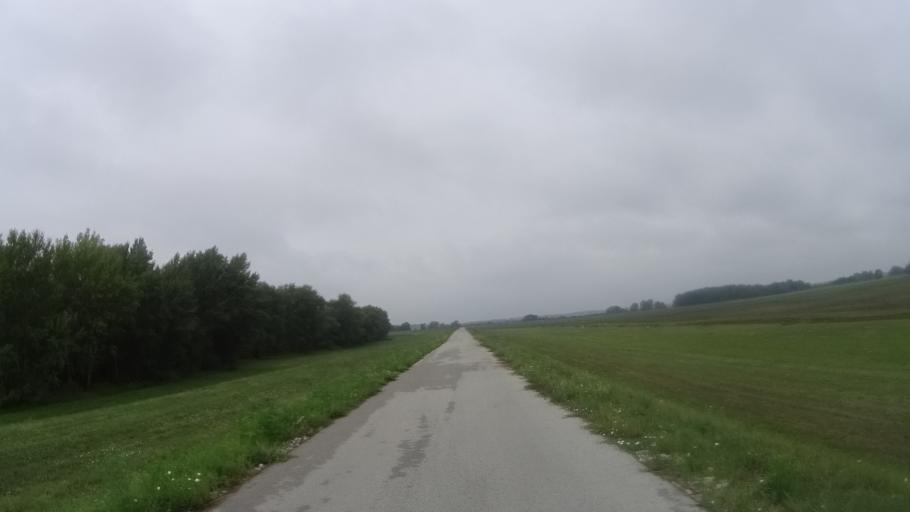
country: HU
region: Komarom-Esztergom
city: Almasfuzito
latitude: 47.7472
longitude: 18.2130
